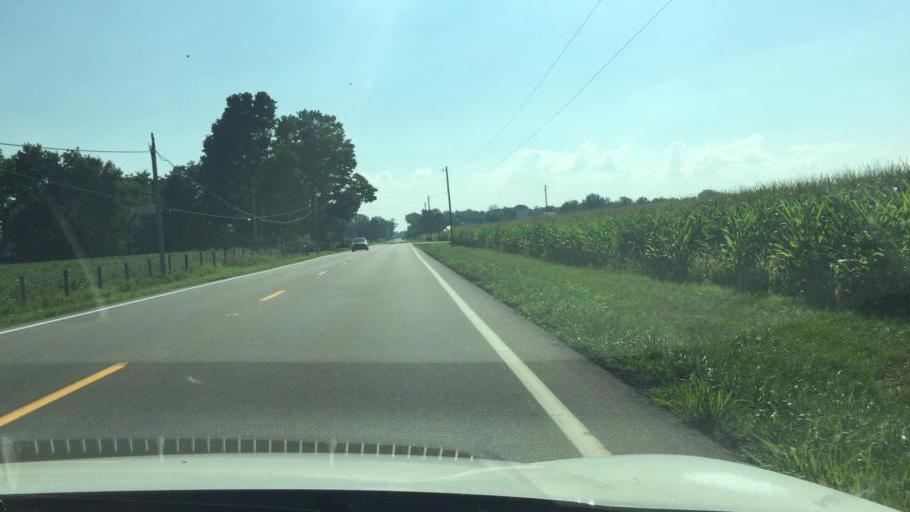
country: US
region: Ohio
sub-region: Clark County
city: Northridge
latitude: 40.0166
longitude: -83.6808
